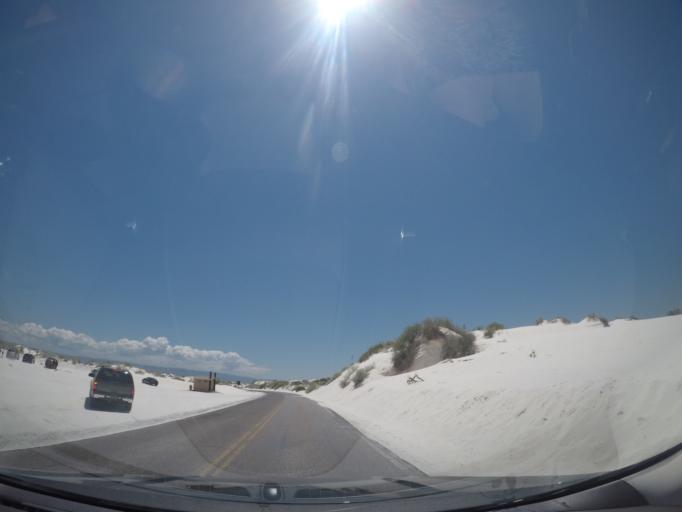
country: US
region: New Mexico
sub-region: Otero County
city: Holloman Air Force Base
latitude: 32.7934
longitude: -106.2396
